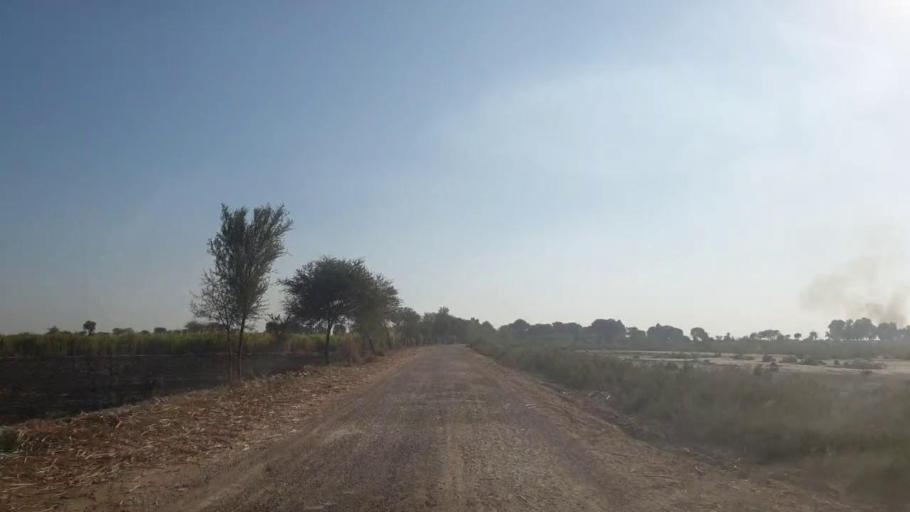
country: PK
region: Sindh
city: Mirwah Gorchani
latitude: 25.4252
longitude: 69.1653
